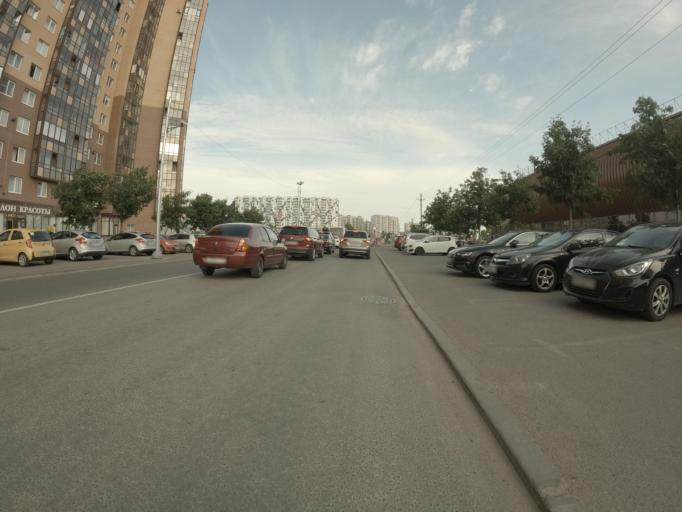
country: RU
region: St.-Petersburg
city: Krasnogvargeisky
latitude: 59.9131
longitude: 30.5050
